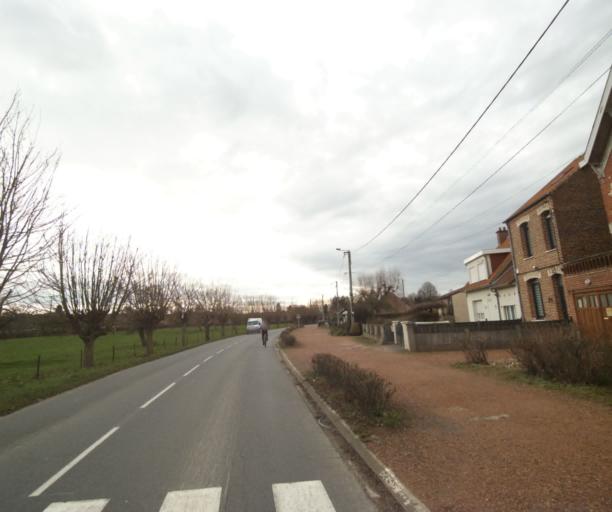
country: FR
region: Nord-Pas-de-Calais
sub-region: Departement du Nord
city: Sebourg
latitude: 50.3441
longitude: 3.6396
